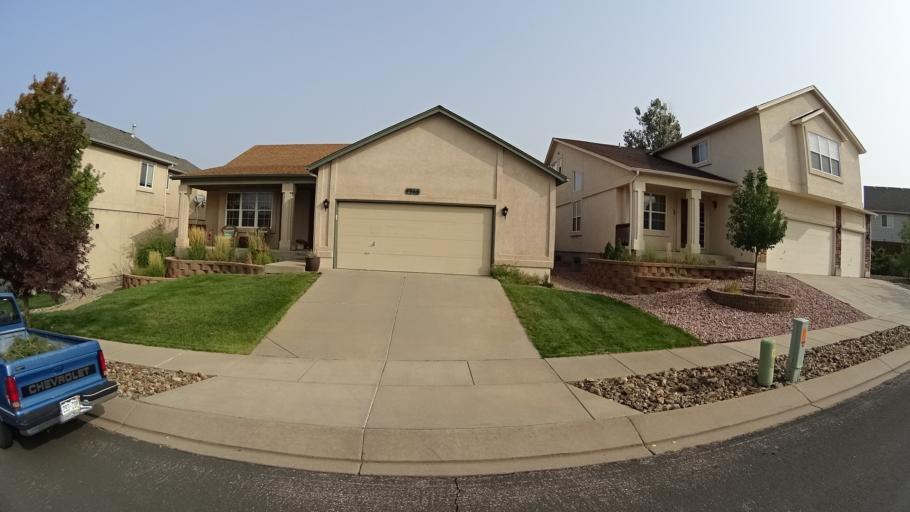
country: US
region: Colorado
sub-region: El Paso County
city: Cimarron Hills
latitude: 38.9306
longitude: -104.7344
